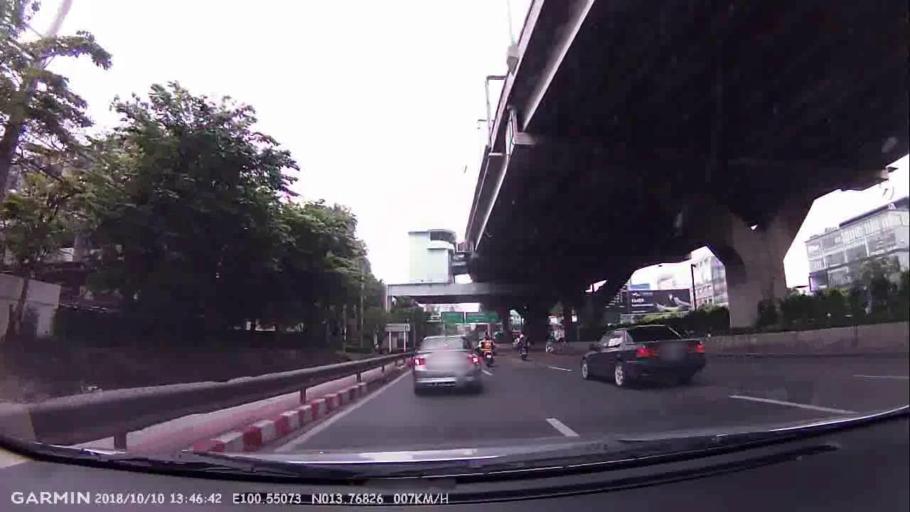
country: TH
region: Bangkok
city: Din Daeng
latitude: 13.7683
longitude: 100.5507
